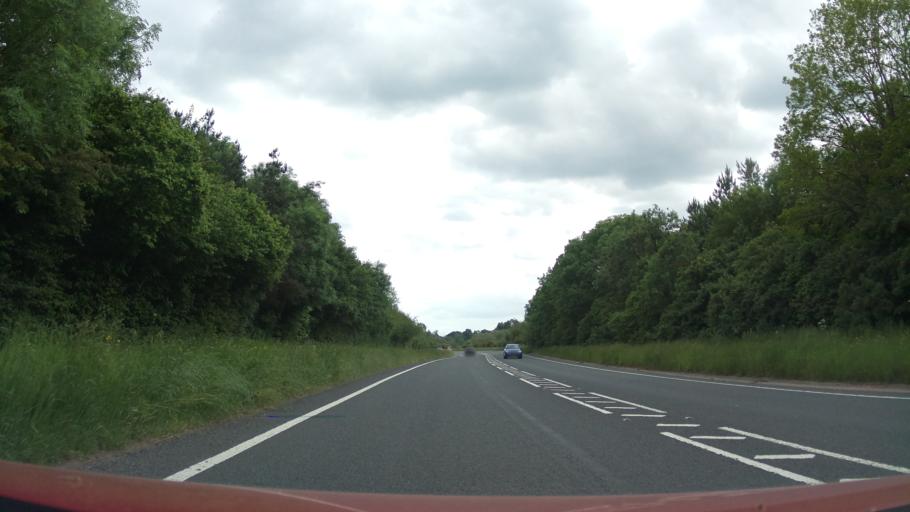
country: GB
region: England
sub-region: Worcestershire
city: Worcester
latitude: 52.1748
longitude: -2.2492
